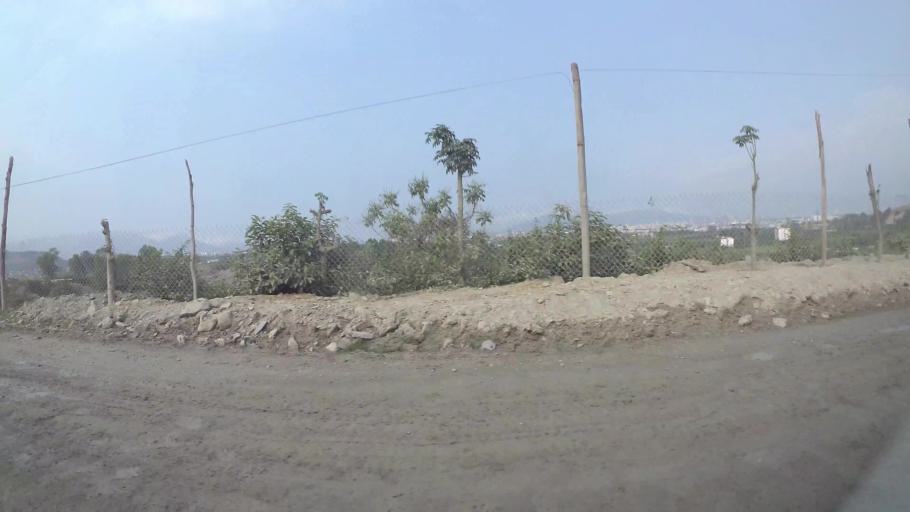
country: VN
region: Da Nang
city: Lien Chieu
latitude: 16.0408
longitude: 108.1508
